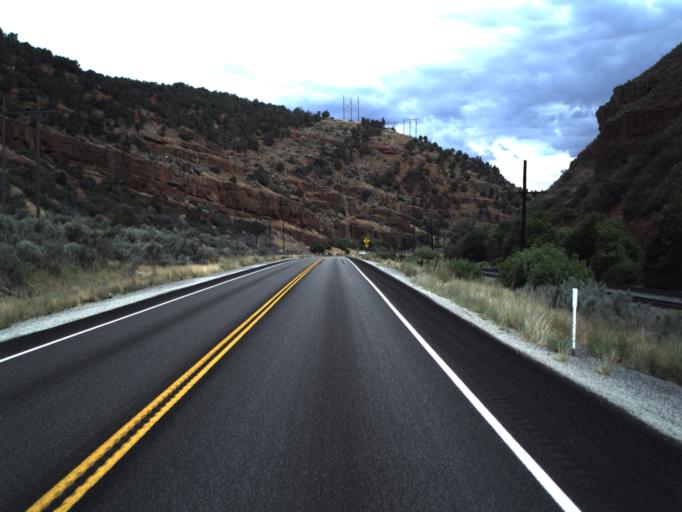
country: US
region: Utah
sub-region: Utah County
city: Mapleton
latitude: 39.9912
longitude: -111.3823
